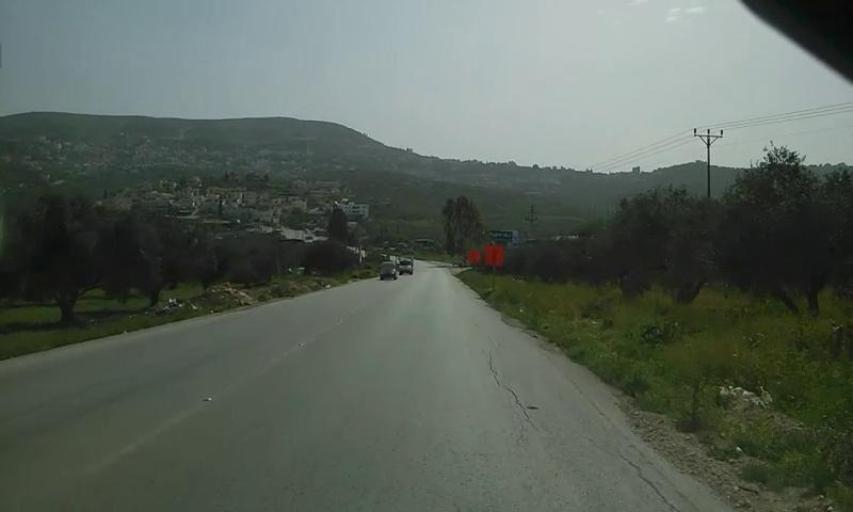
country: PS
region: West Bank
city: Al Fandaqumiyah
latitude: 32.3354
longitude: 35.2061
